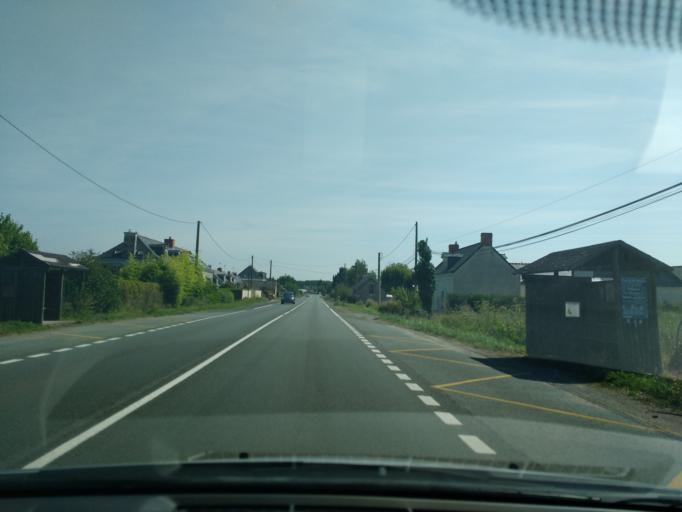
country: FR
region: Pays de la Loire
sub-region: Departement de Maine-et-Loire
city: Corne
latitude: 47.4745
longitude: -0.3305
